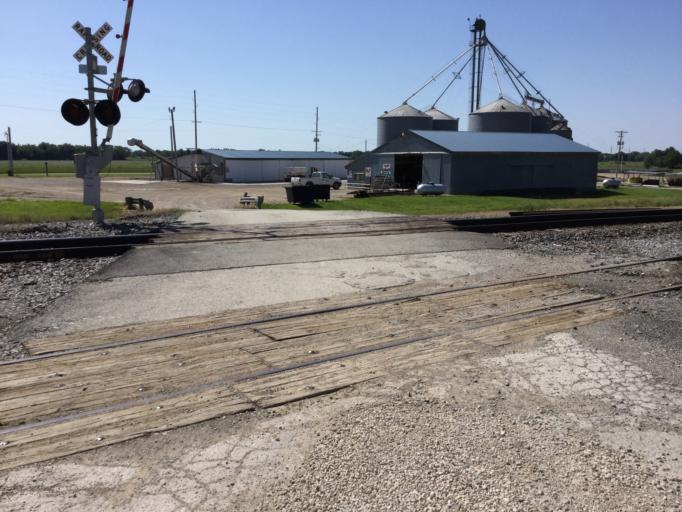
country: US
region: Kansas
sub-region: Anderson County
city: Garnett
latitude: 38.0796
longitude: -95.1518
